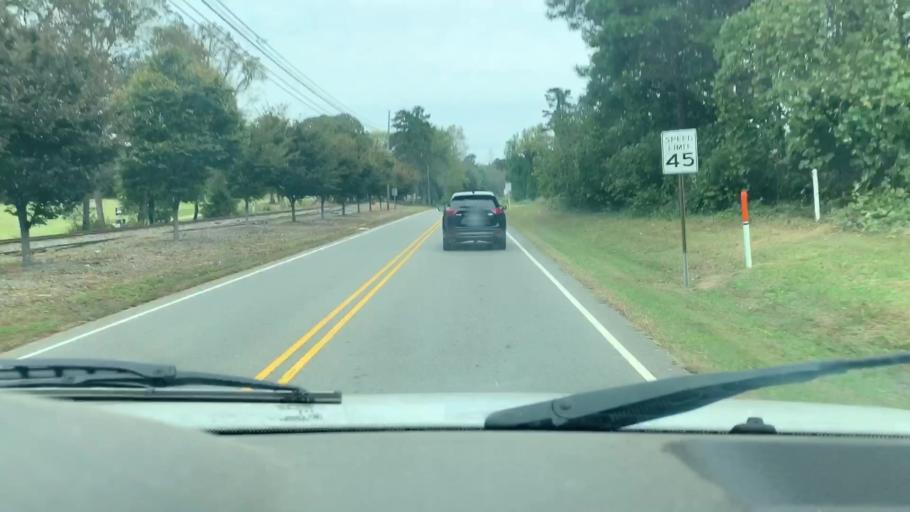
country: US
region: North Carolina
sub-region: Iredell County
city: Mooresville
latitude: 35.5681
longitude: -80.8278
